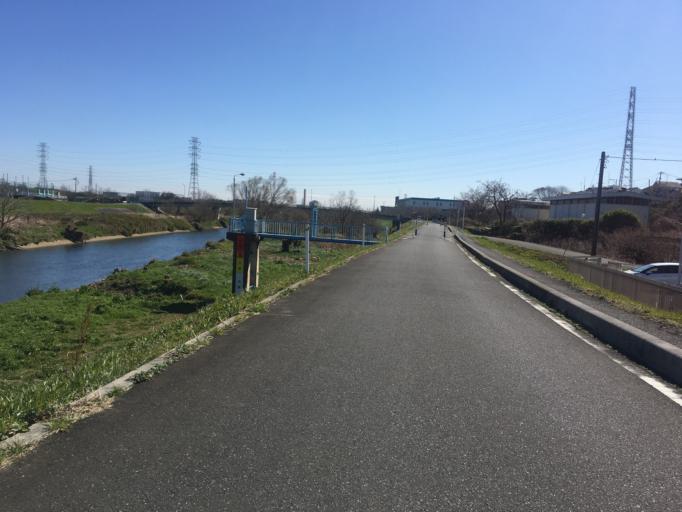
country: JP
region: Saitama
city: Shiki
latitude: 35.8287
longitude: 139.5912
